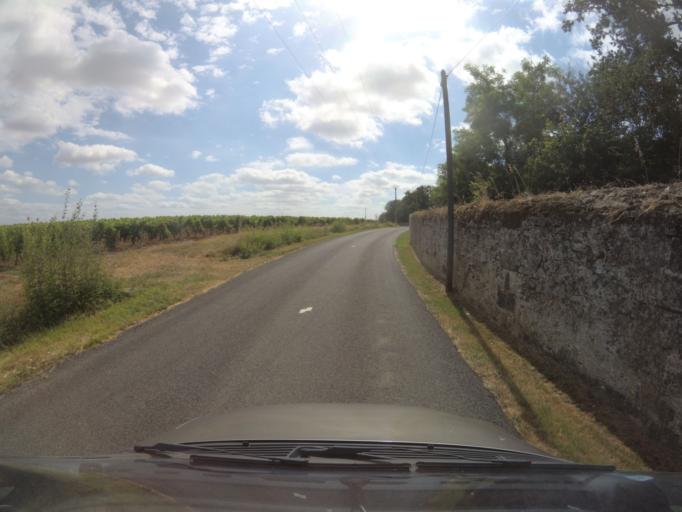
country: FR
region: Pays de la Loire
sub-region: Departement de Maine-et-Loire
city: Saint-Jean
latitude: 47.1926
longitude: -0.3642
